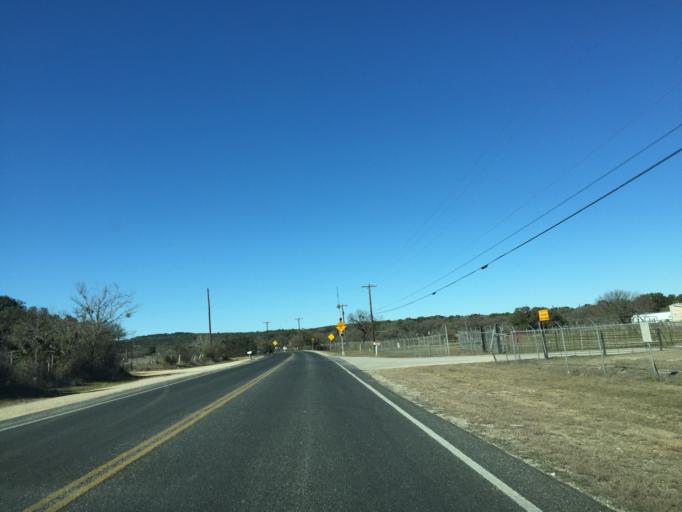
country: US
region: Texas
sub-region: Comal County
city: Bulverde
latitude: 29.7463
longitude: -98.4066
